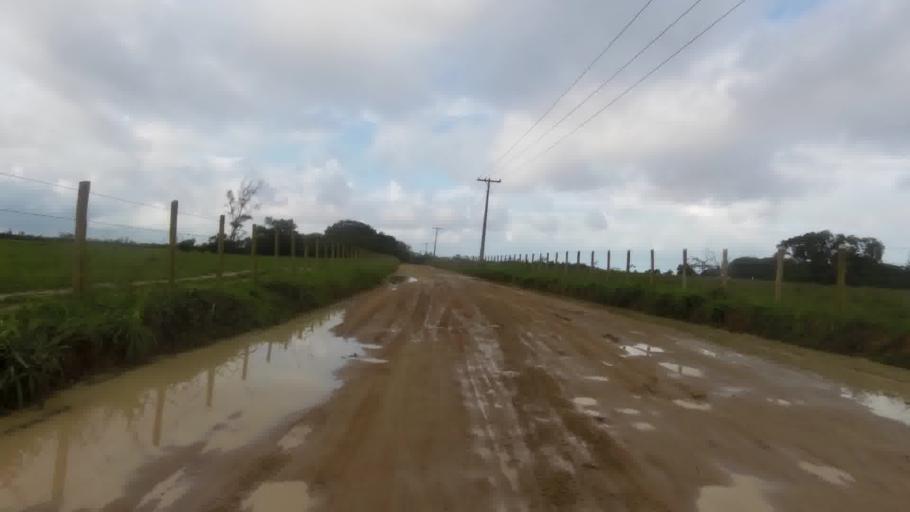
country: BR
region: Espirito Santo
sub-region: Piuma
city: Piuma
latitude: -20.7754
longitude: -40.6303
